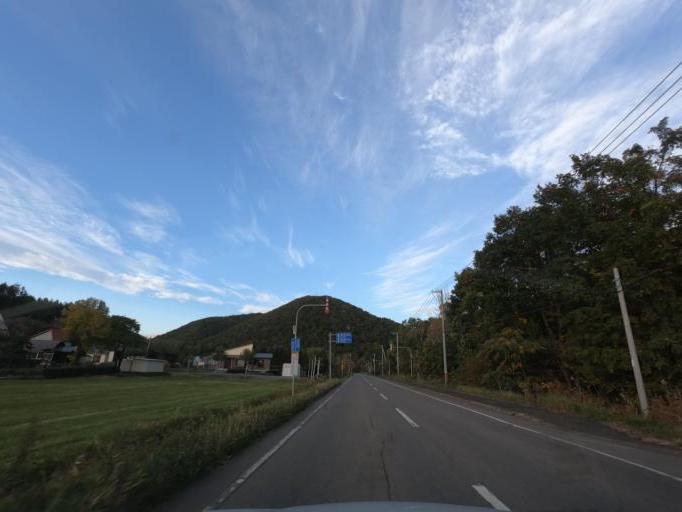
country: JP
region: Hokkaido
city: Obihiro
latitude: 42.5752
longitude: 143.3100
